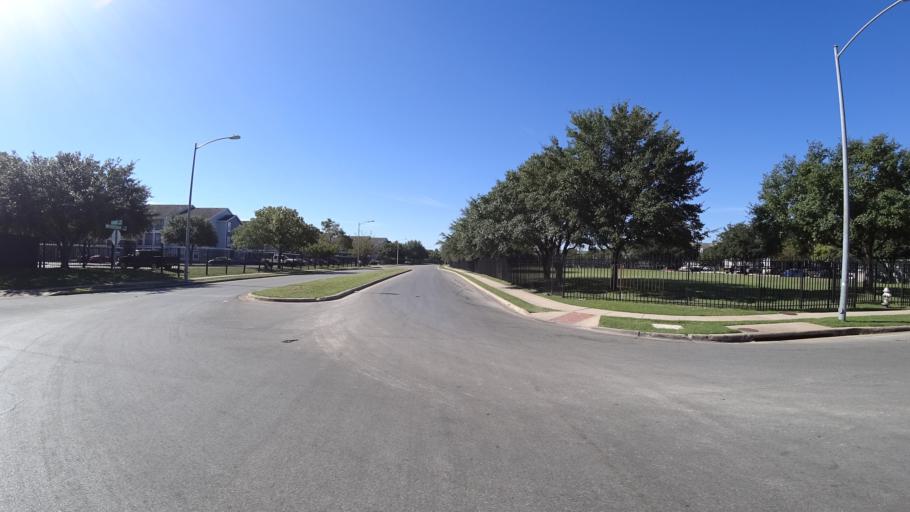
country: US
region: Texas
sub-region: Travis County
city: Austin
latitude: 30.2376
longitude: -97.7172
